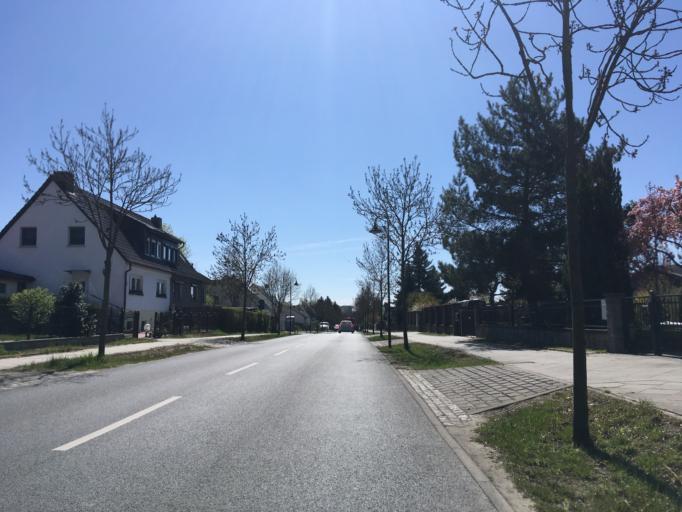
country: DE
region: Brandenburg
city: Bernau bei Berlin
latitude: 52.6781
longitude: 13.5543
